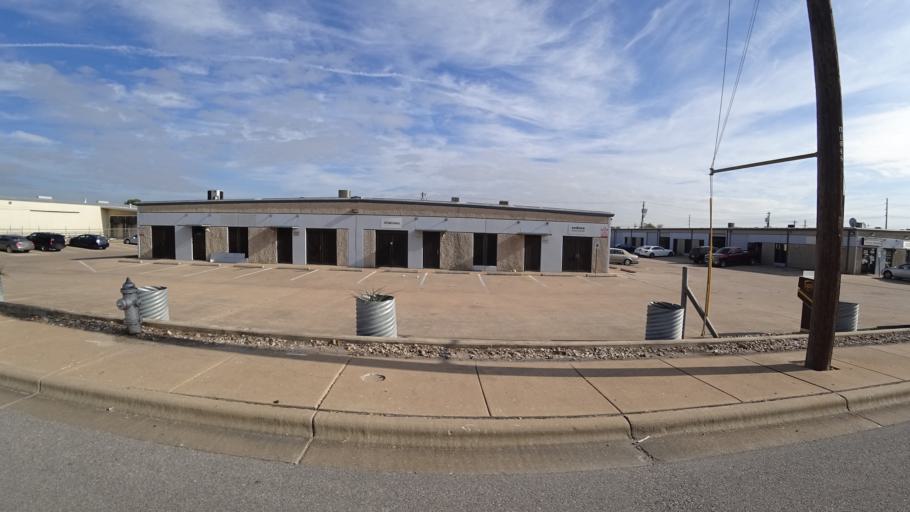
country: US
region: Texas
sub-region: Travis County
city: Austin
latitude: 30.2106
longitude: -97.7270
